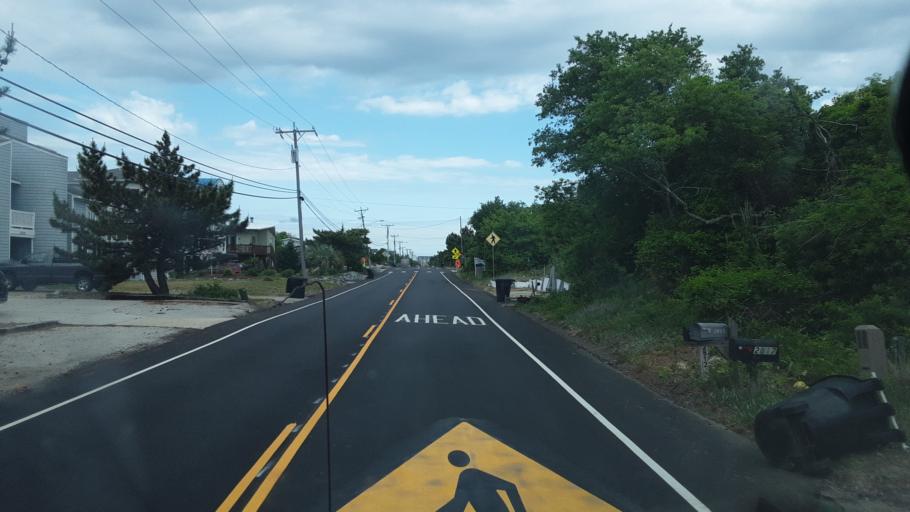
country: US
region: Virginia
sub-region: City of Virginia Beach
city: Virginia Beach
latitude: 36.7322
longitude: -75.9400
